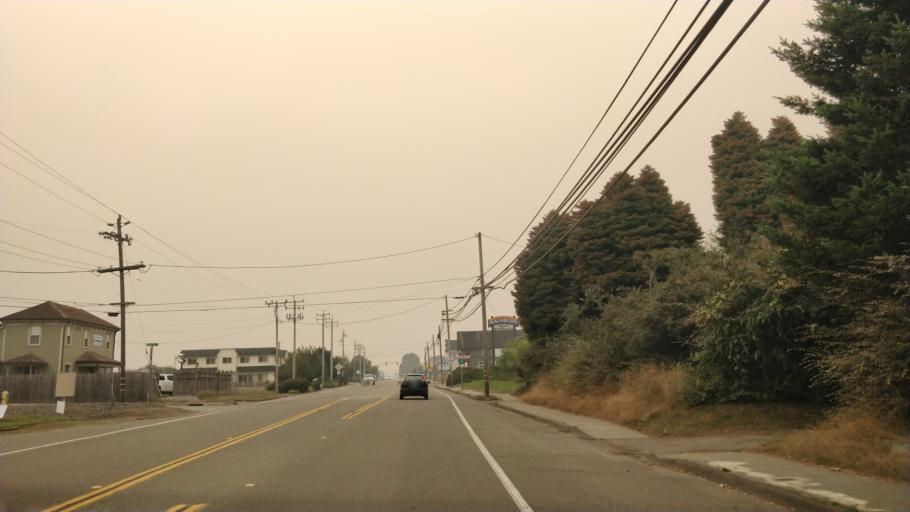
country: US
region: California
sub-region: Humboldt County
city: McKinleyville
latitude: 40.9495
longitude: -124.1009
